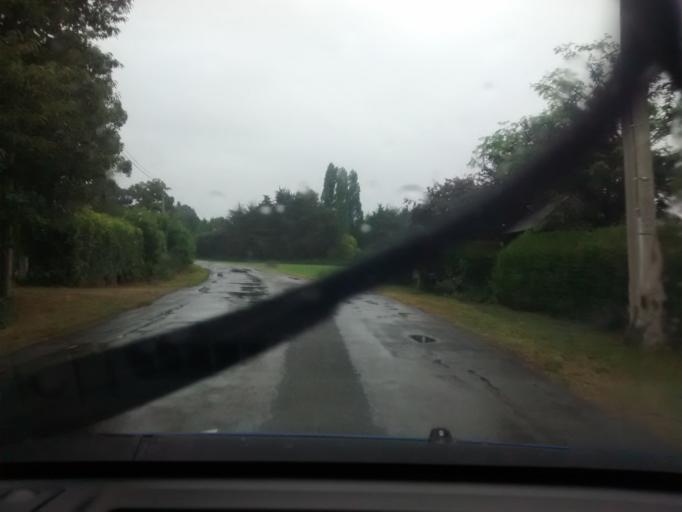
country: FR
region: Brittany
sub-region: Departement d'Ille-et-Vilaine
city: Betton
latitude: 48.1748
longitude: -1.6230
